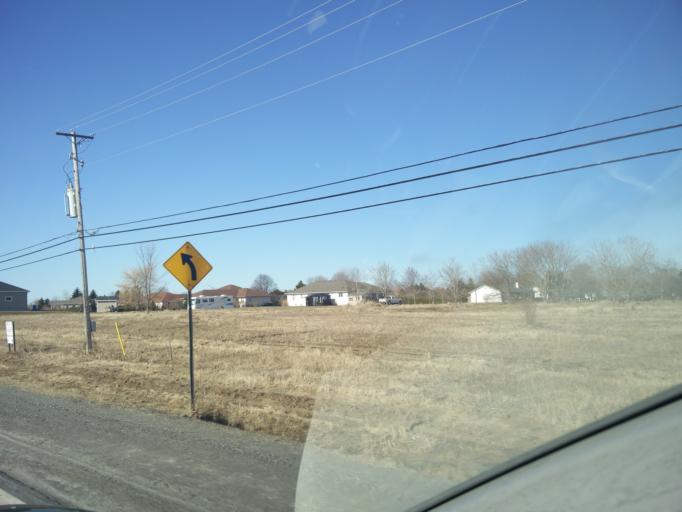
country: CA
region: Ontario
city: Bells Corners
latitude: 45.1424
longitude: -75.7139
